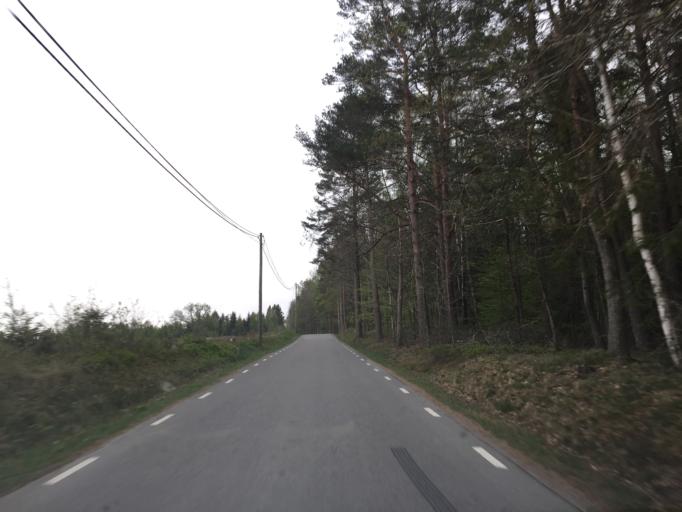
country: SE
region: Vaestra Goetaland
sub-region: Ale Kommun
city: Surte
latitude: 57.8284
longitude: 11.9907
